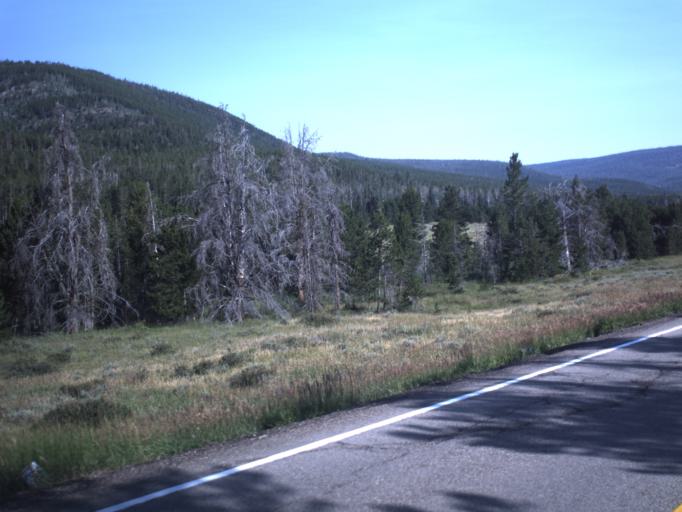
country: US
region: Utah
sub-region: Uintah County
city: Maeser
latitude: 40.7704
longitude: -109.4712
